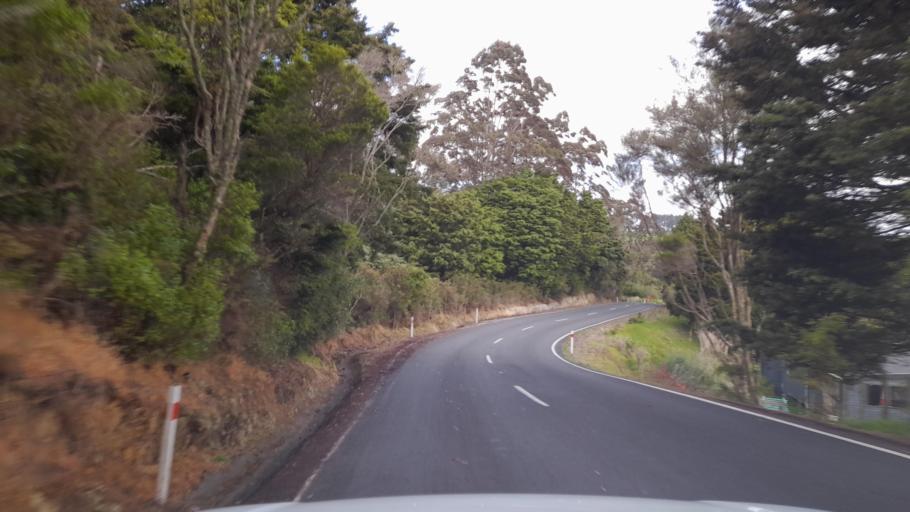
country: NZ
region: Northland
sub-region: Whangarei
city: Maungatapere
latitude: -35.7701
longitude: 174.2444
